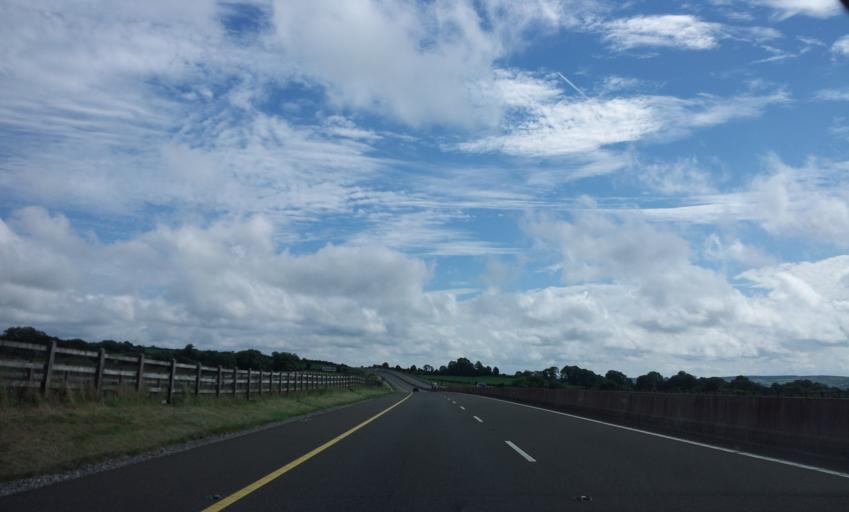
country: IE
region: Munster
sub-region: North Tipperary
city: Roscrea
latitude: 52.9103
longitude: -7.8470
